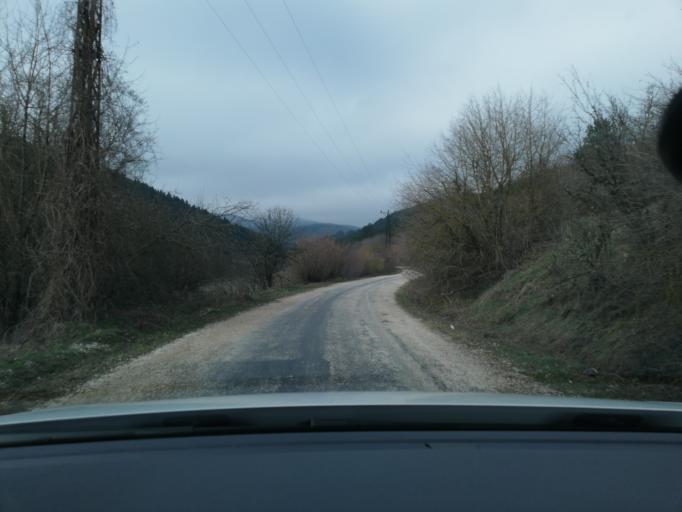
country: TR
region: Bolu
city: Bolu
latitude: 40.6851
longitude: 31.4665
